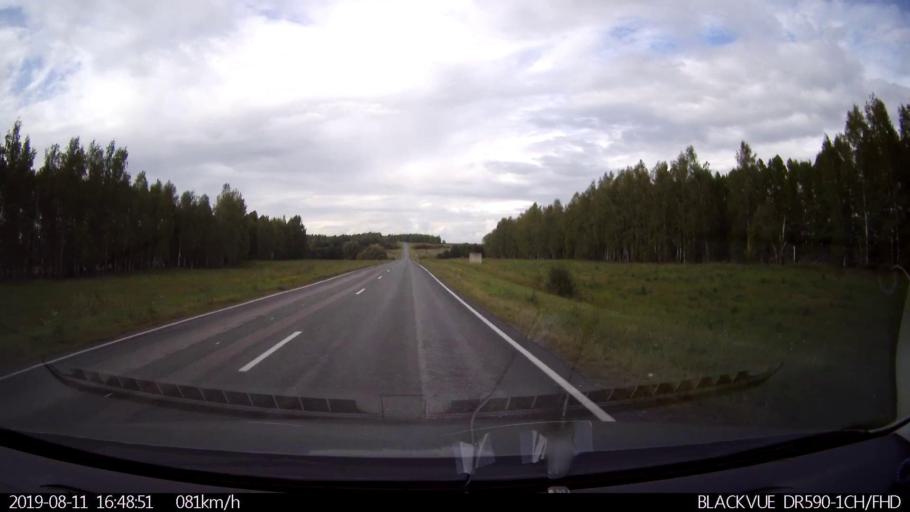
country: RU
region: Ulyanovsk
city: Mayna
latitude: 54.2141
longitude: 47.6938
